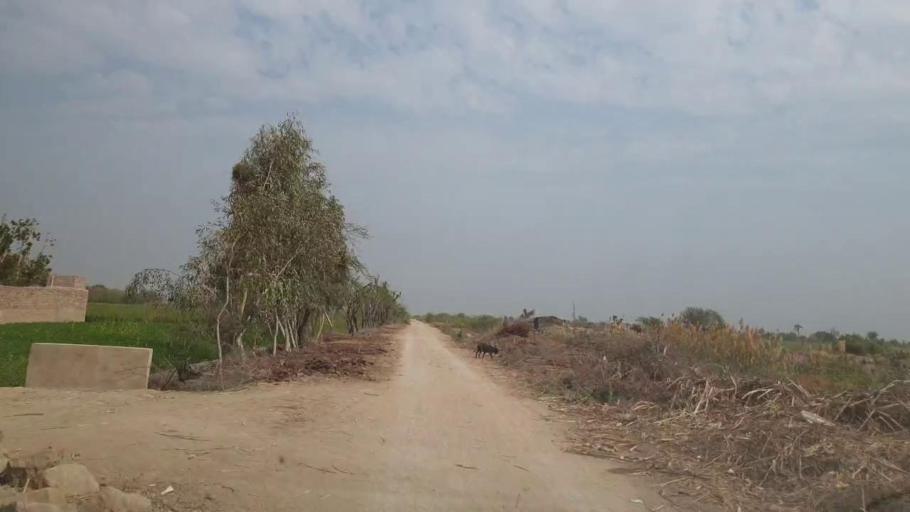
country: PK
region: Sindh
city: Mirpur Khas
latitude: 25.5403
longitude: 69.1307
